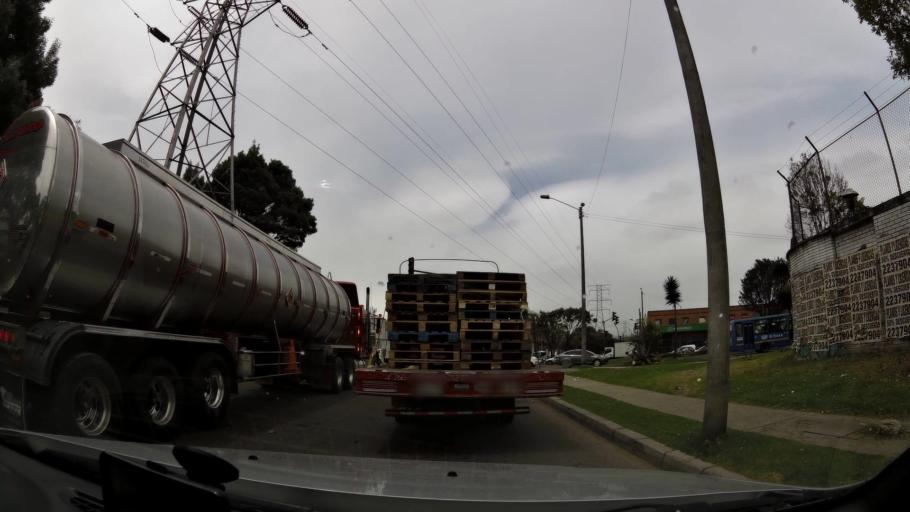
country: CO
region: Bogota D.C.
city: Bogota
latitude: 4.6396
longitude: -74.1223
